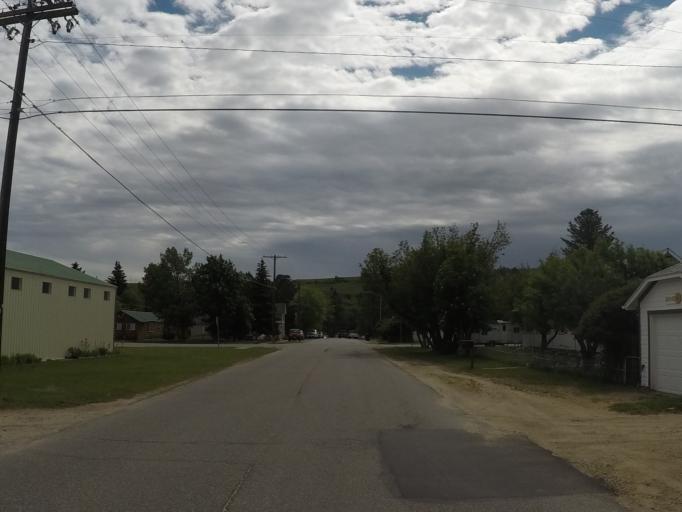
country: US
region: Montana
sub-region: Carbon County
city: Red Lodge
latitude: 45.1789
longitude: -109.2529
